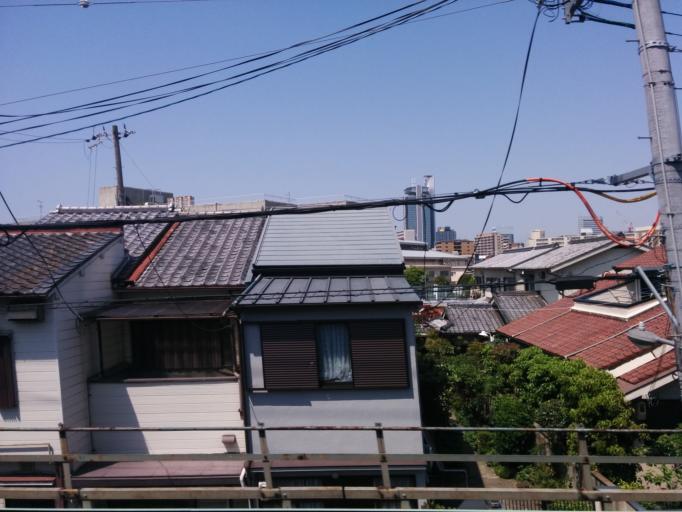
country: JP
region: Osaka
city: Osaka-shi
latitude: 34.7263
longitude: 135.5104
